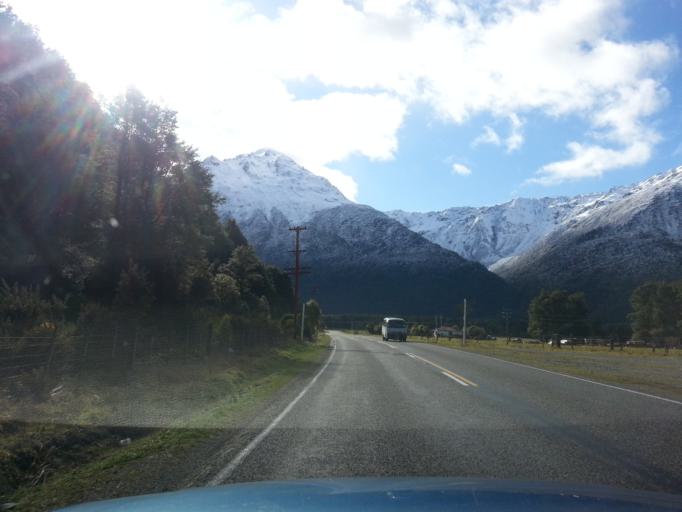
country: NZ
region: West Coast
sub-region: Grey District
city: Greymouth
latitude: -42.7719
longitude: 171.6248
